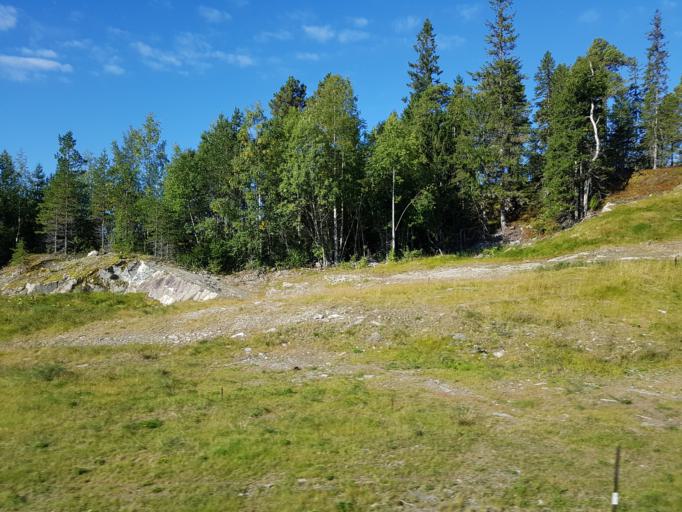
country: NO
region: Sor-Trondelag
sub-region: Trondheim
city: Trondheim
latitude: 63.6095
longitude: 10.2379
